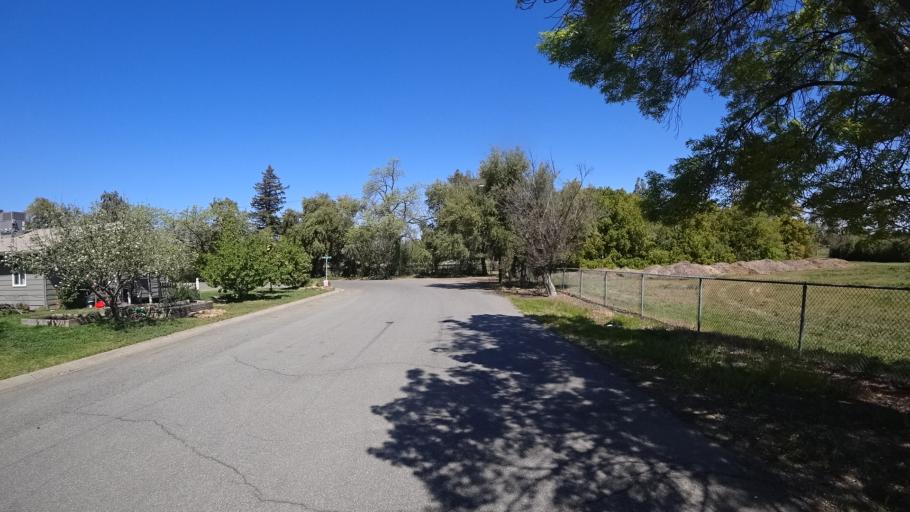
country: US
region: California
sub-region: Glenn County
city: Willows
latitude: 39.5216
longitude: -122.1847
